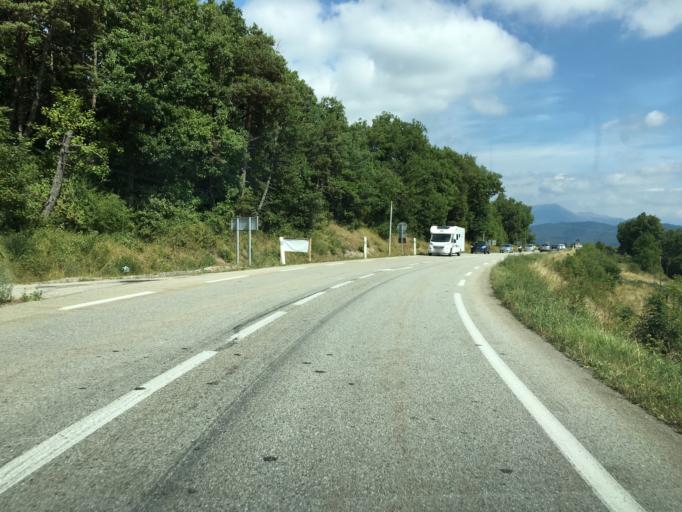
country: FR
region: Rhone-Alpes
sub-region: Departement de l'Isere
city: Mens
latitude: 44.7738
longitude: 5.6596
